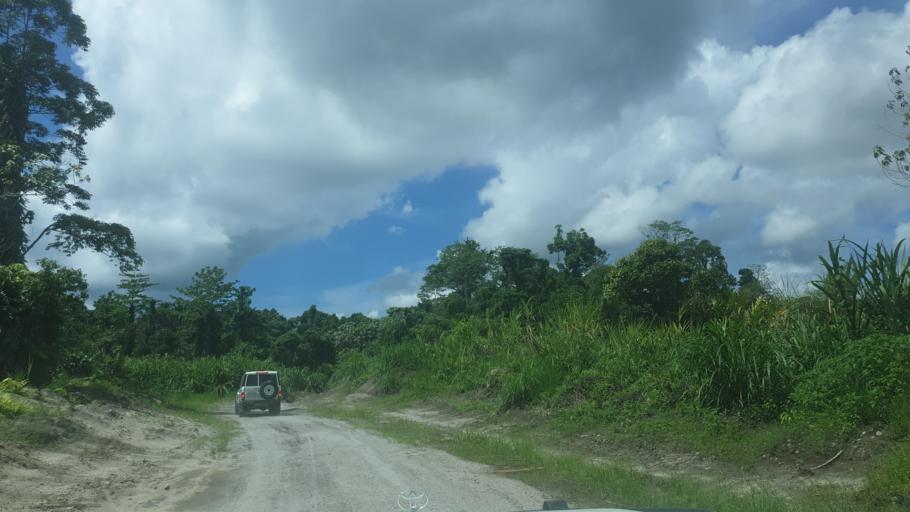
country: PG
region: Bougainville
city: Panguna
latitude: -6.7391
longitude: 155.5026
